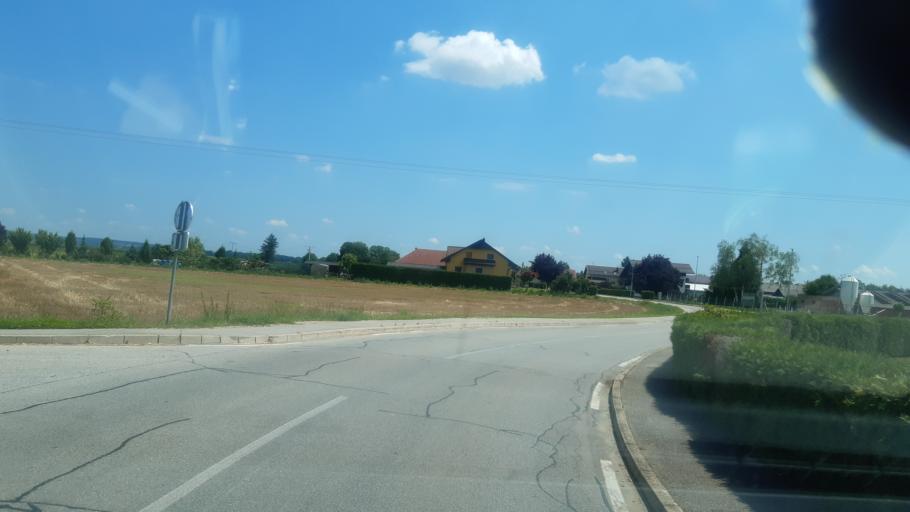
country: SI
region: Moravske Toplice
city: Moravske Toplice
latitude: 46.6705
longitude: 16.2169
